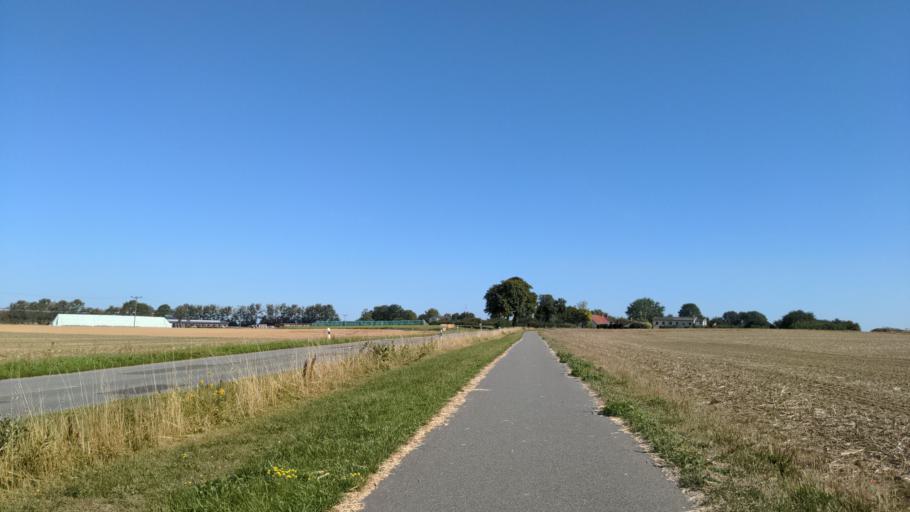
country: DE
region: Mecklenburg-Vorpommern
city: Gramkow
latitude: 53.9390
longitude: 11.3310
